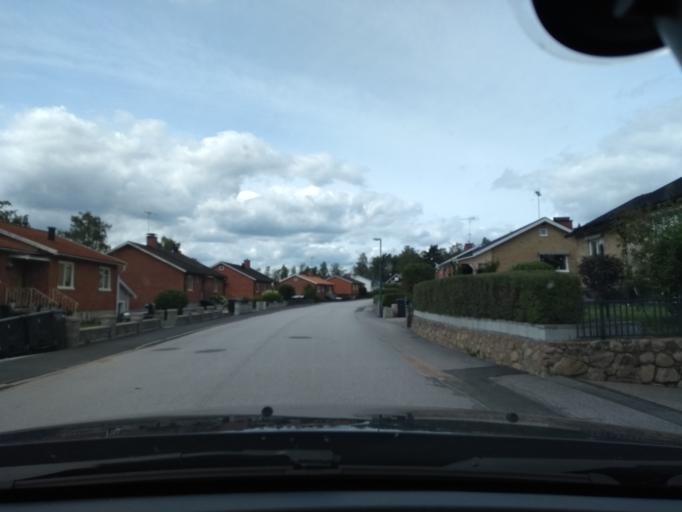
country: SE
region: Kalmar
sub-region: Vimmerby Kommun
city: Vimmerby
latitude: 57.6767
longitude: 15.8560
